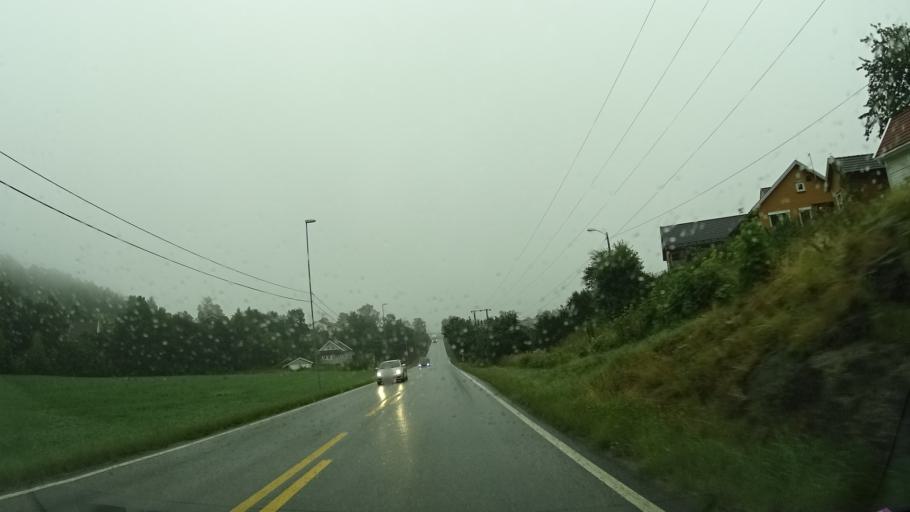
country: NO
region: Aust-Agder
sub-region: Lillesand
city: Lillesand
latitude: 58.2556
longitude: 8.3774
